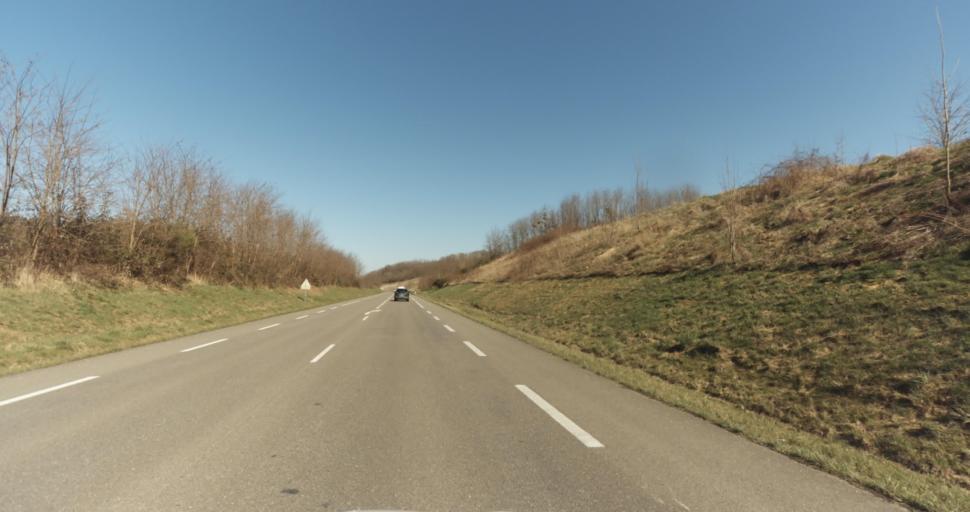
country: FR
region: Franche-Comte
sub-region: Departement du Jura
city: Montmorot
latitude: 46.6687
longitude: 5.5069
